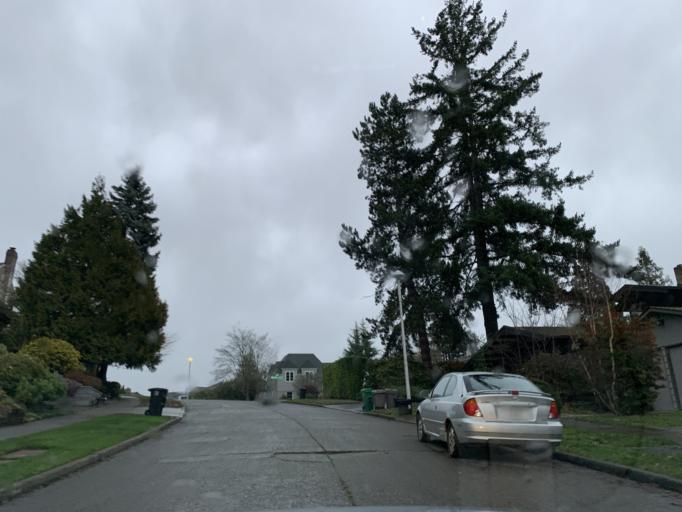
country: US
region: Washington
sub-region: King County
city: Yarrow Point
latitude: 47.6706
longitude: -122.2759
